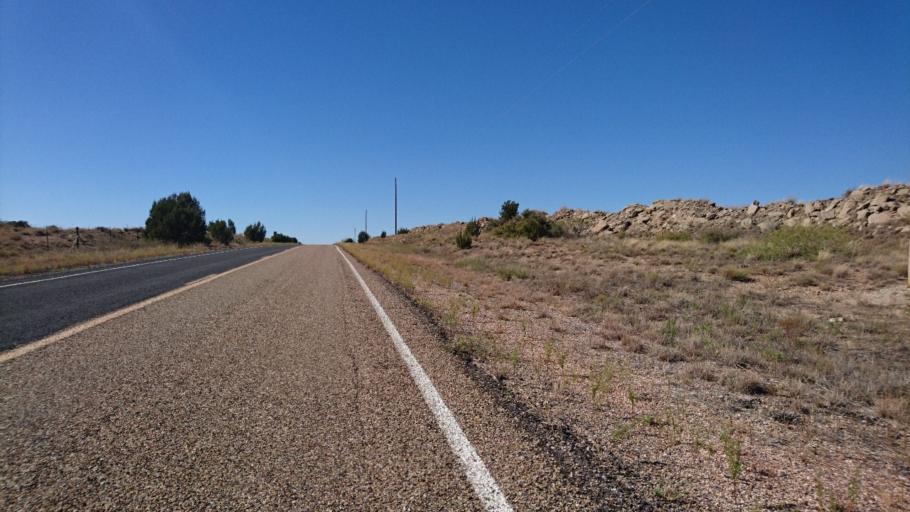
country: US
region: New Mexico
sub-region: Quay County
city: Tucumcari
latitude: 35.0682
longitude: -104.1988
